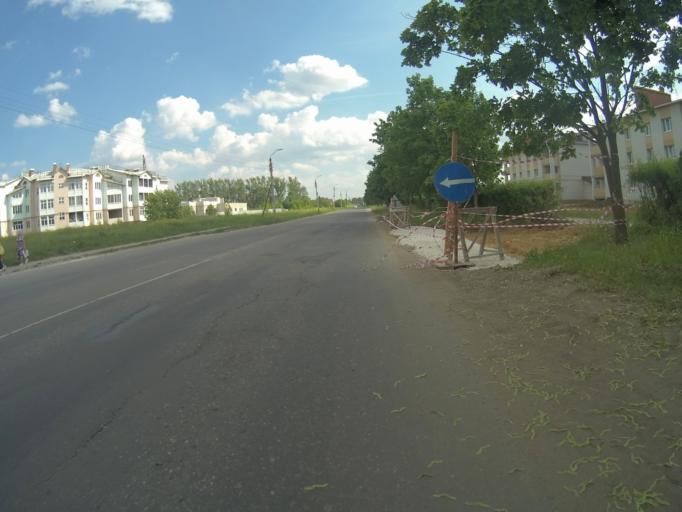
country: RU
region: Vladimir
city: Suzdal'
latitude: 56.4332
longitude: 40.4529
